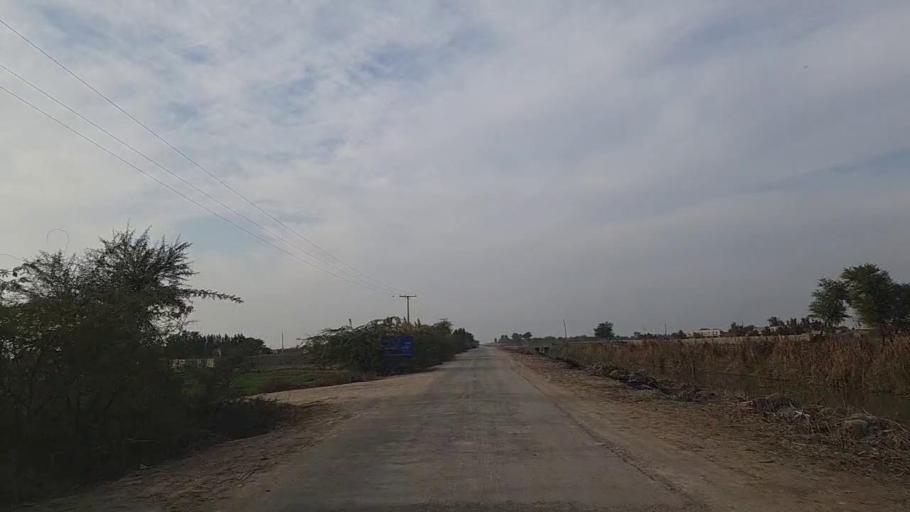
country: PK
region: Sindh
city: Daur
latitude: 26.4901
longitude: 68.4595
